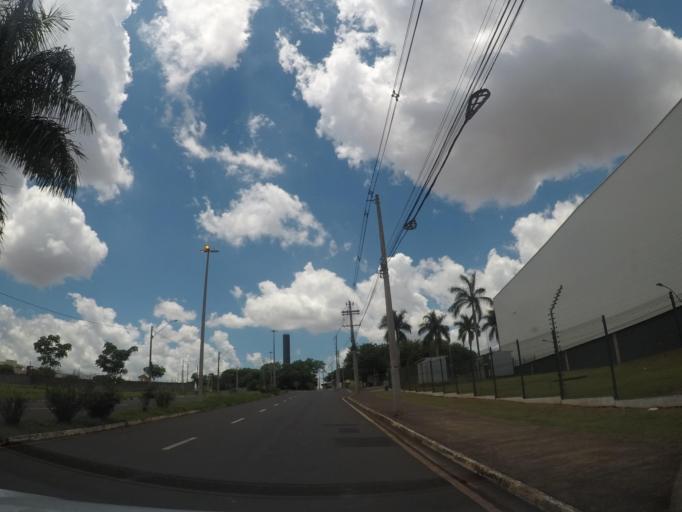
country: BR
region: Sao Paulo
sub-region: Hortolandia
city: Hortolandia
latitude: -22.8280
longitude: -47.2175
